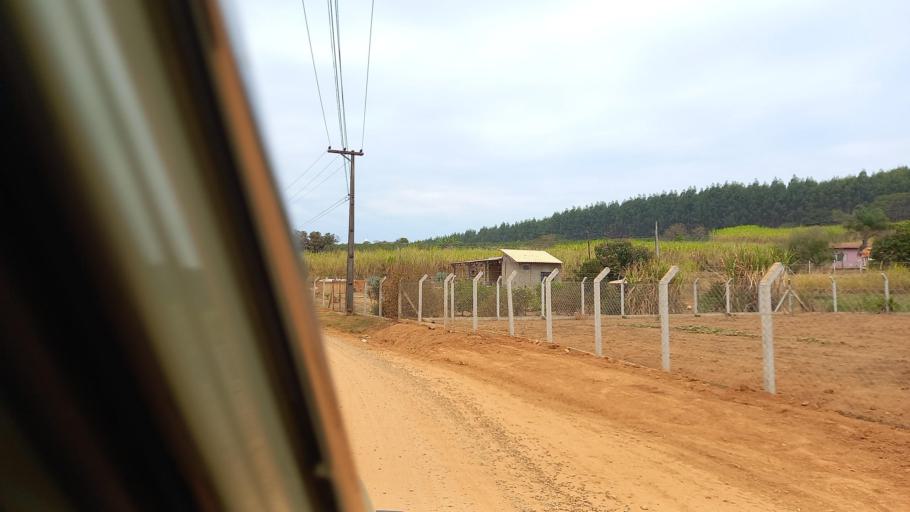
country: BR
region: Sao Paulo
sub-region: Moji-Guacu
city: Mogi-Gaucu
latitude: -22.3226
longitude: -46.8574
